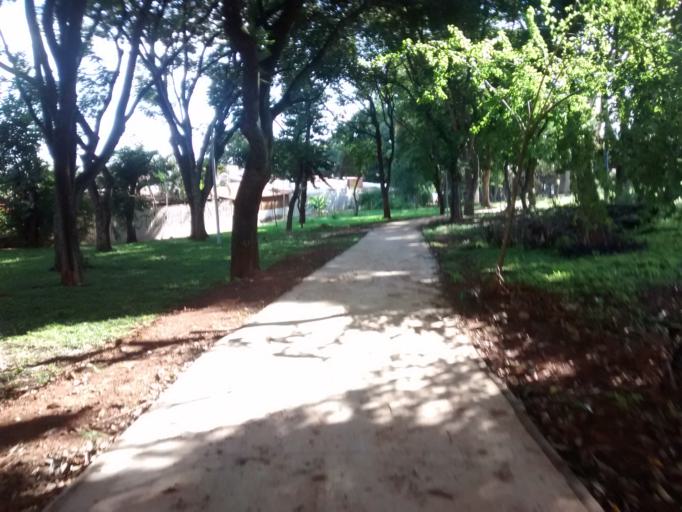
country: BR
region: Federal District
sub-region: Brasilia
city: Brasilia
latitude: -15.7617
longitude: -47.8941
